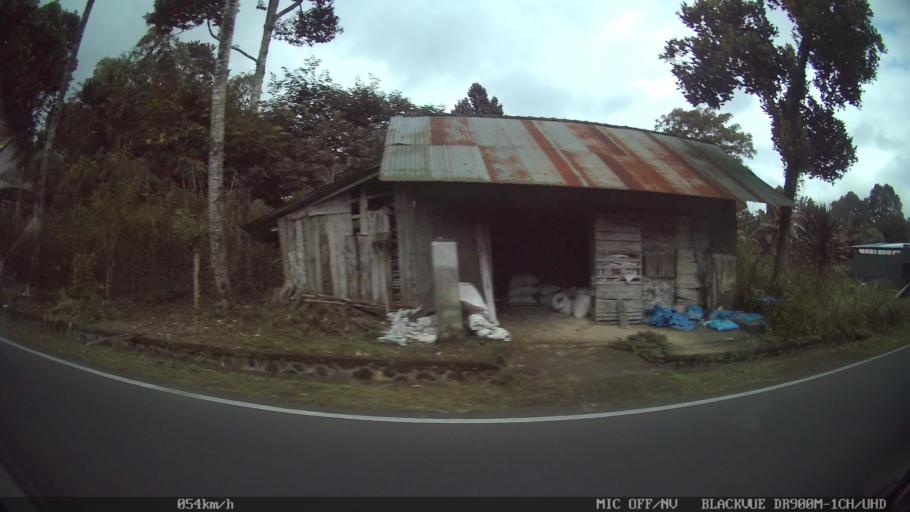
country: ID
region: Bali
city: Banjar Tiga
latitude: -8.3804
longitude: 115.4178
